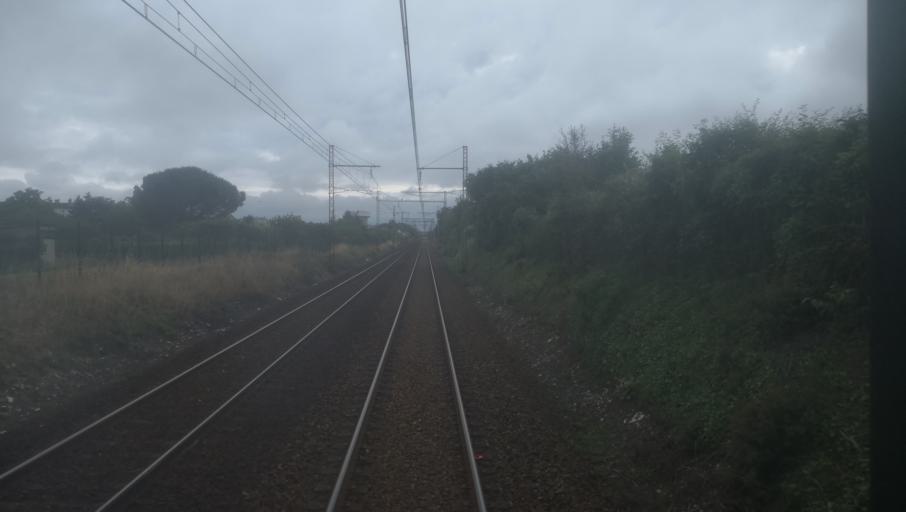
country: FR
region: Centre
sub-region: Departement de l'Indre
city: Chateauroux
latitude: 46.7995
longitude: 1.6752
